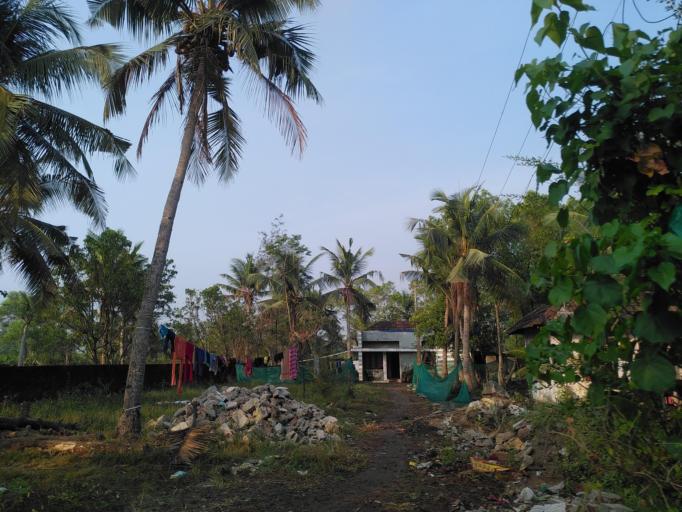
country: IN
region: Kerala
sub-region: Alappuzha
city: Arukutti
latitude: 9.9243
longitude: 76.3290
